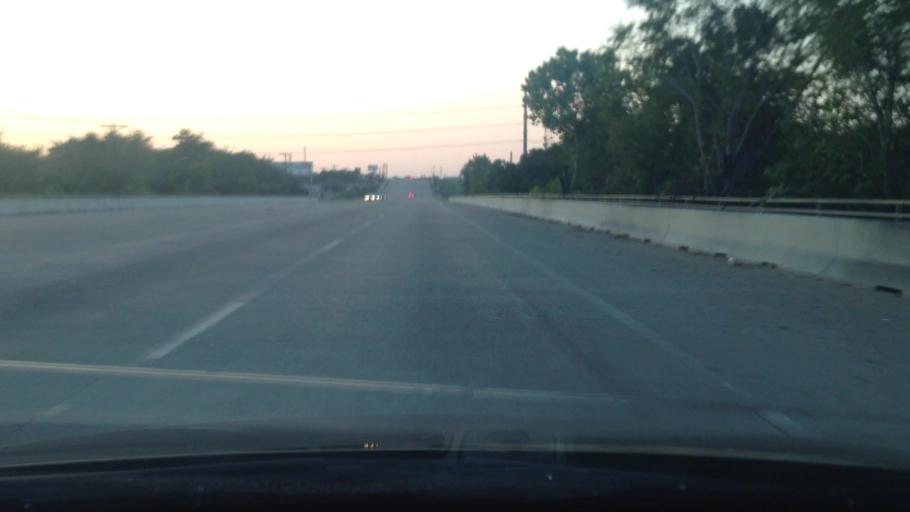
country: US
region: Texas
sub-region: Tarrant County
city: Kennedale
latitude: 32.6592
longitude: -97.2346
